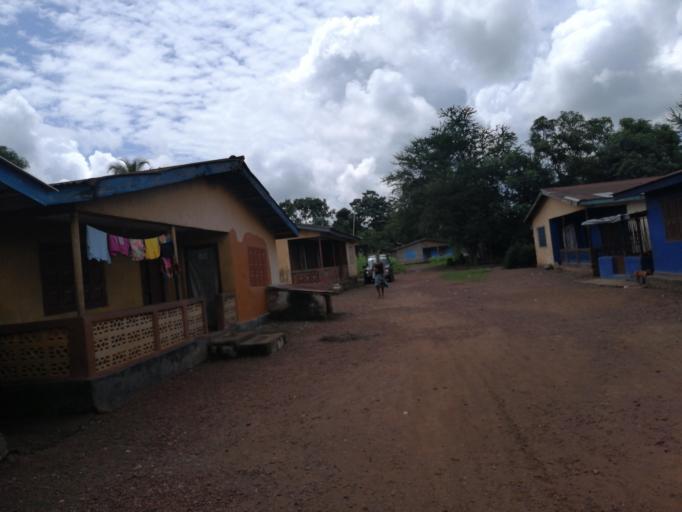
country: SL
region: Northern Province
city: Port Loko
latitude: 8.7751
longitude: -12.7881
